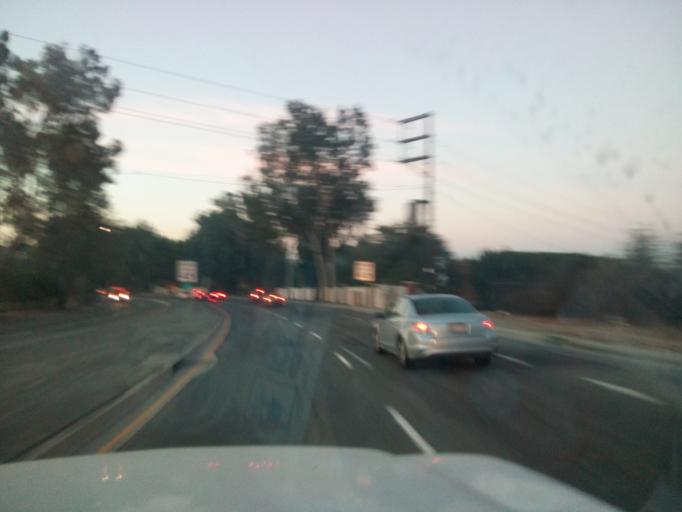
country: US
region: California
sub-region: Los Angeles County
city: Whittier
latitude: 33.9648
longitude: -118.0018
